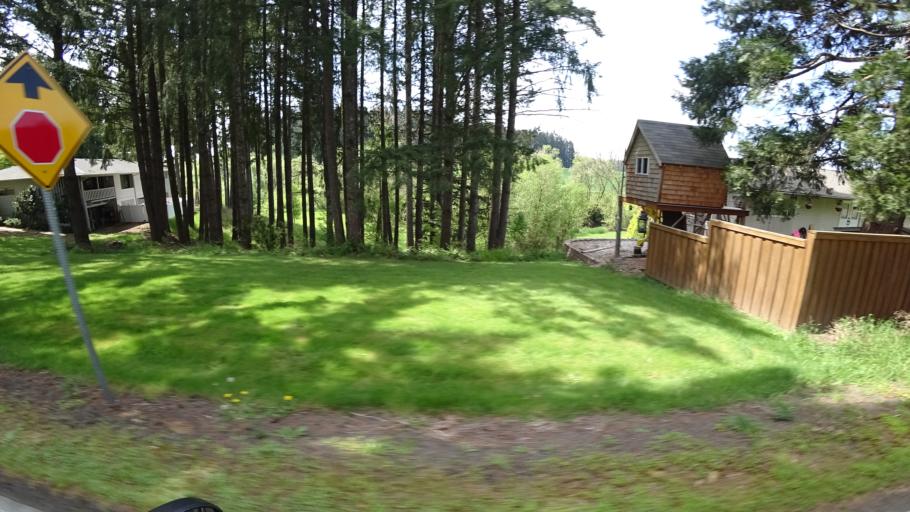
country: US
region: Oregon
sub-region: Washington County
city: Hillsboro
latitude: 45.5403
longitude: -122.9993
